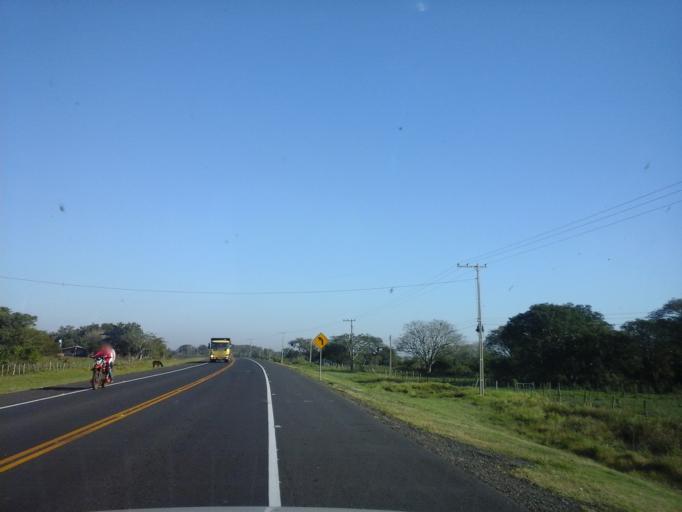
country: PY
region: Neembucu
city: Pilar
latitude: -26.8694
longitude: -58.1138
